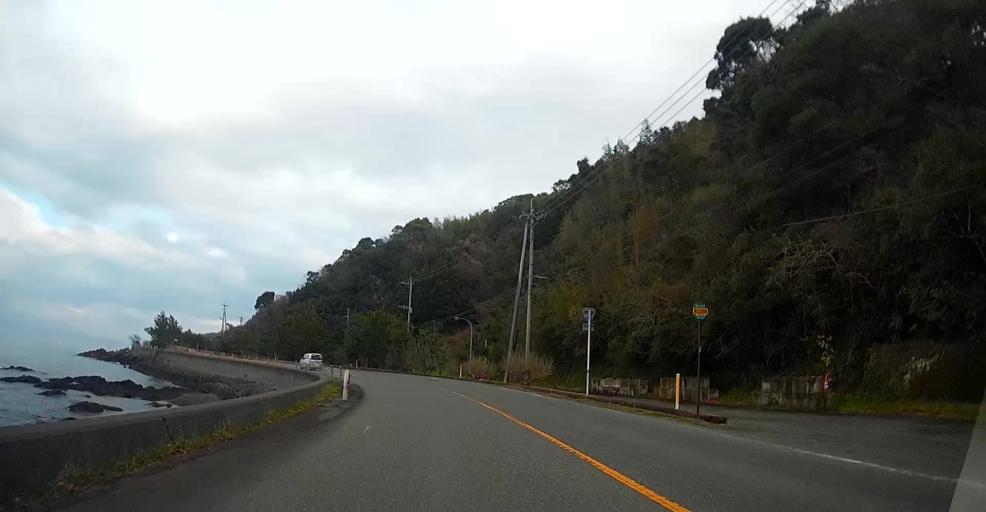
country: JP
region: Kumamoto
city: Hondo
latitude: 32.4886
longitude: 130.2899
